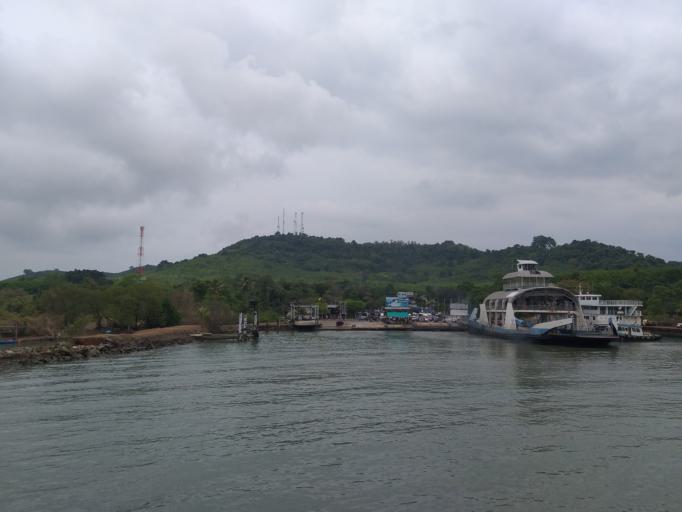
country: TH
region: Trat
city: Laem Ngop
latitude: 12.1857
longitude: 102.3015
